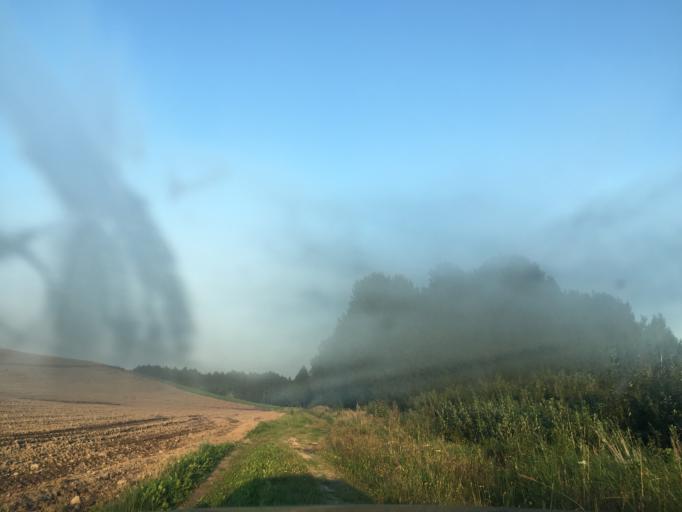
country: LV
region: Limbazu Rajons
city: Limbazi
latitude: 57.5747
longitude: 24.7778
